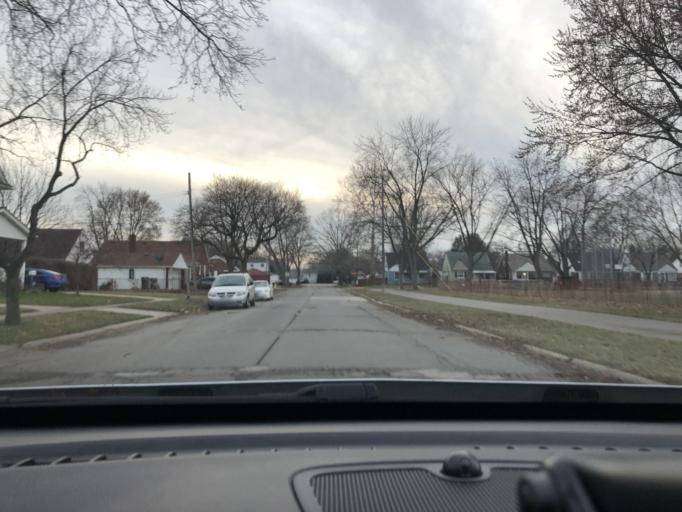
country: US
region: Michigan
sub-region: Wayne County
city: Allen Park
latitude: 42.2824
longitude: -83.2228
